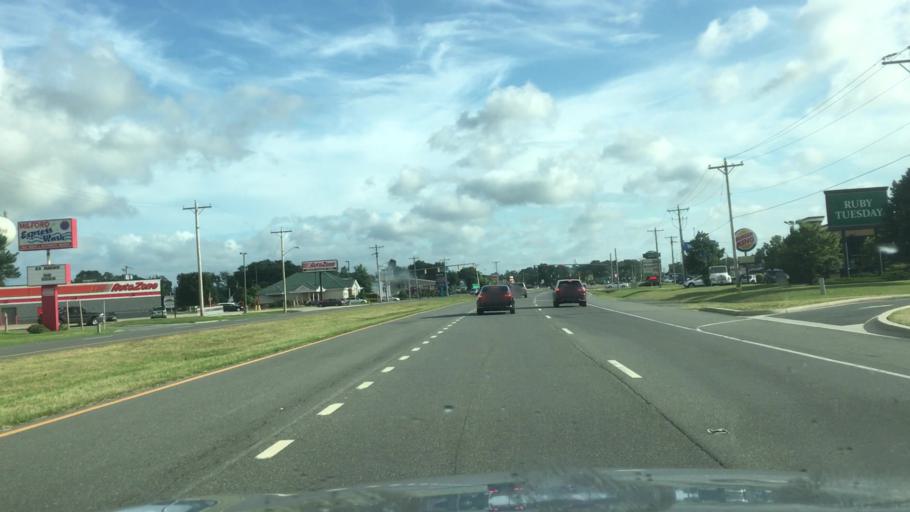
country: US
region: Delaware
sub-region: Sussex County
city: Milford
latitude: 38.9313
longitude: -75.4309
